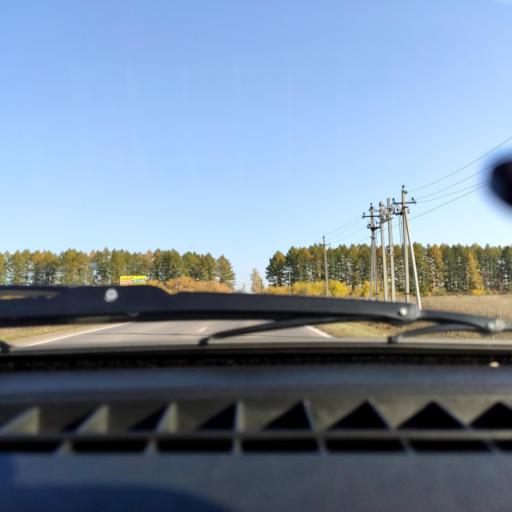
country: RU
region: Bashkortostan
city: Iglino
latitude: 54.7389
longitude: 56.2518
